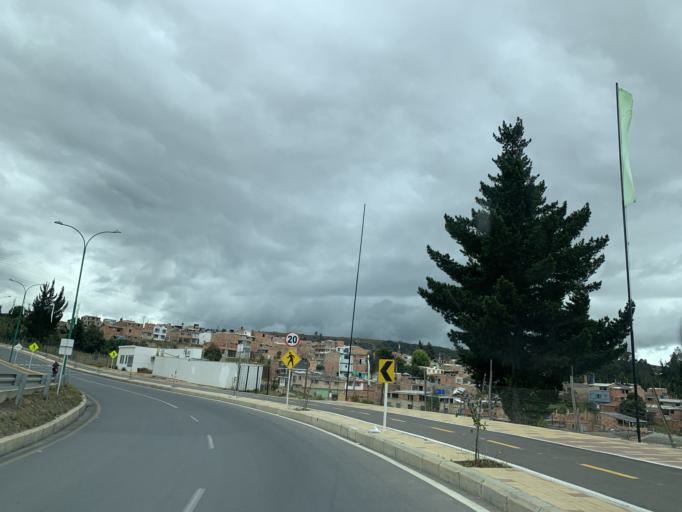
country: CO
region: Boyaca
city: Tunja
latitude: 5.5377
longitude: -73.3480
